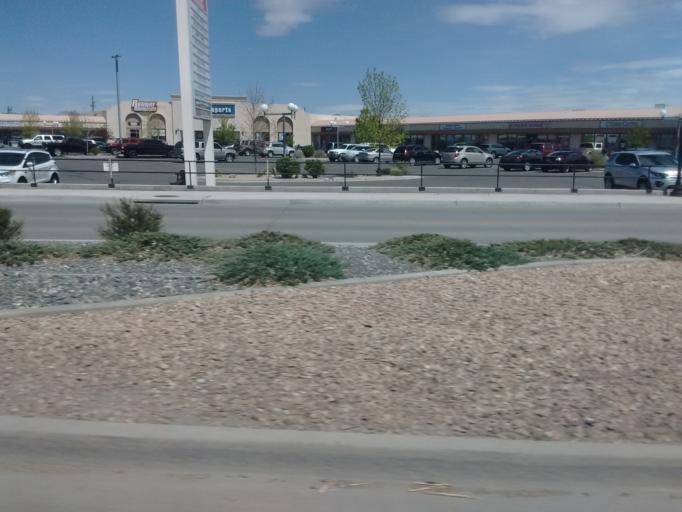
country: US
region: Colorado
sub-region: Mesa County
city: Redlands
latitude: 39.0869
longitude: -108.5975
